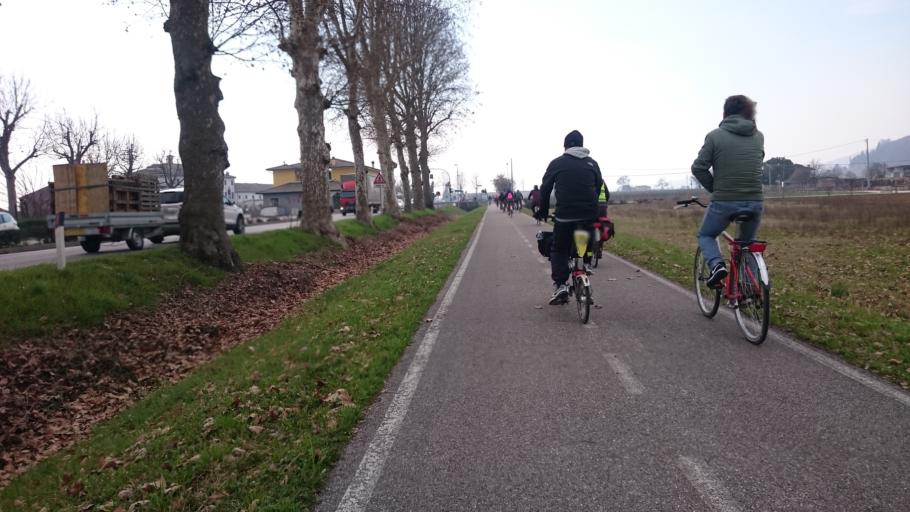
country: IT
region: Veneto
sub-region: Provincia di Vicenza
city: Lumignano
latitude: 45.4551
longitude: 11.6030
